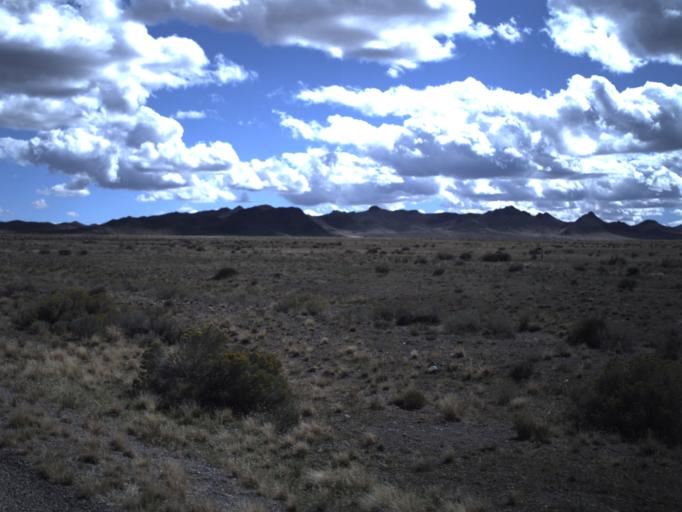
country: US
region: Utah
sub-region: Beaver County
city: Milford
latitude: 38.4507
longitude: -113.3462
